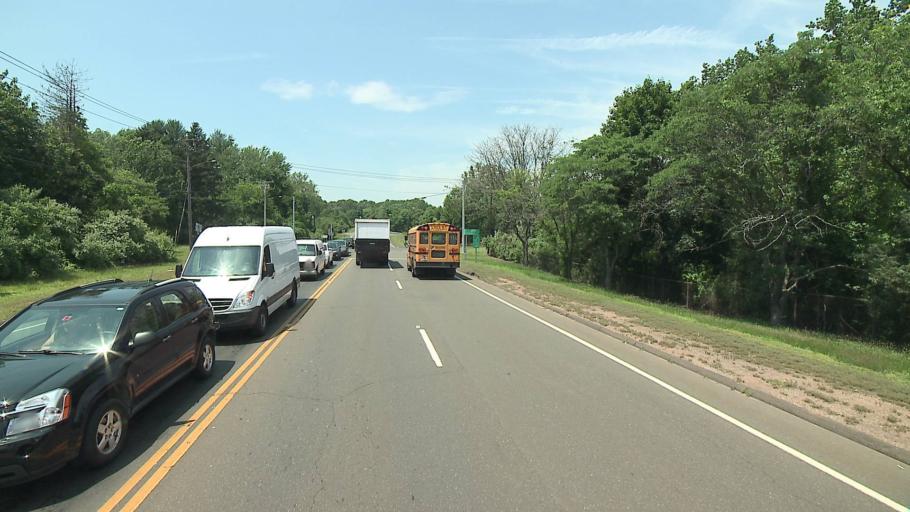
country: US
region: Connecticut
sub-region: New Haven County
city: Hamden
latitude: 41.3789
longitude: -72.8836
